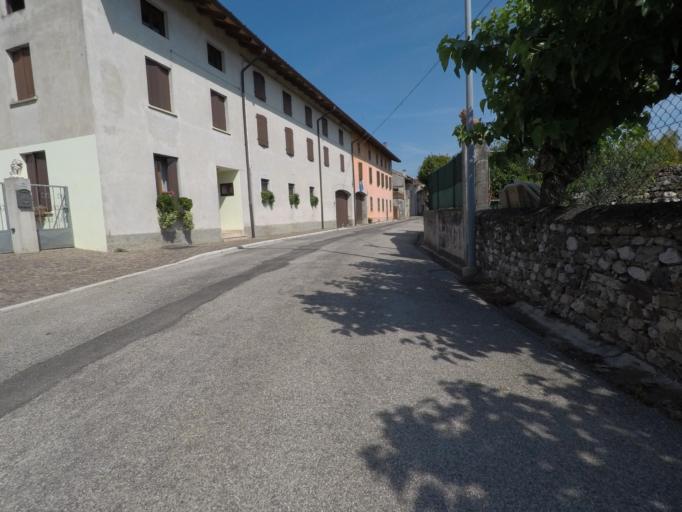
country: IT
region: Friuli Venezia Giulia
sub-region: Provincia di Udine
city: Coseano
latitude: 46.0704
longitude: 13.0230
